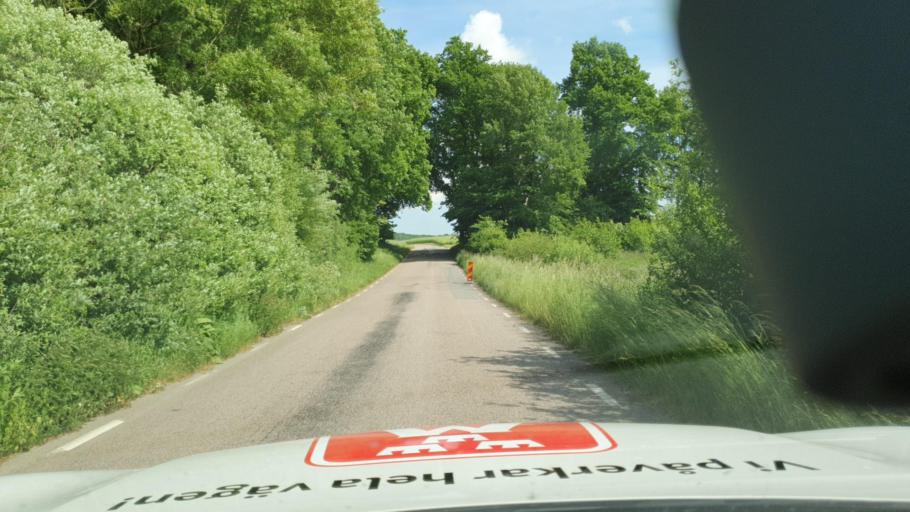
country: SE
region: Skane
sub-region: Svedala Kommun
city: Svedala
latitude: 55.5334
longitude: 13.2010
